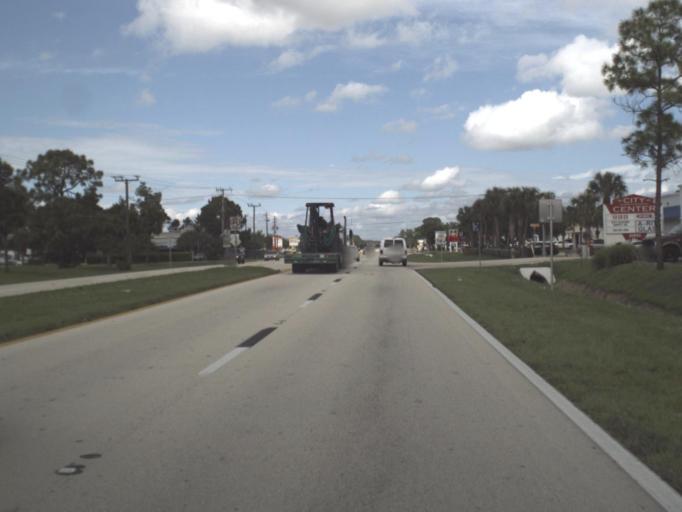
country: US
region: Florida
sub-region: Lee County
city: Villas
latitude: 26.5685
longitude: -81.8530
